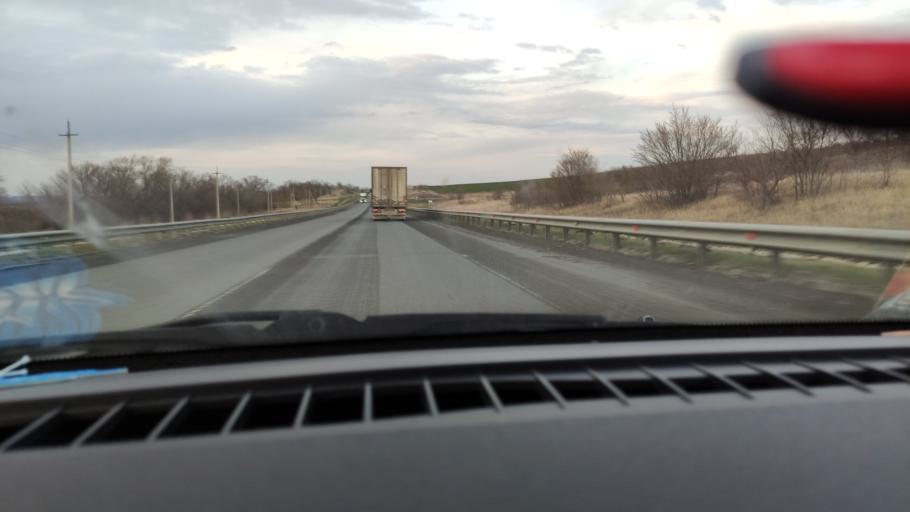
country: RU
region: Saratov
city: Shumeyka
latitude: 51.7847
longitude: 46.1348
